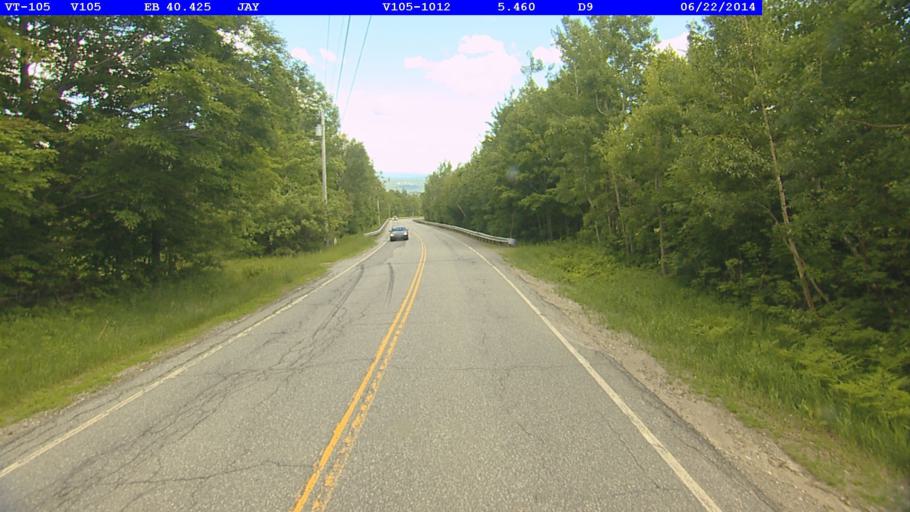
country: CA
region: Quebec
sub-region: Monteregie
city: Sutton
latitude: 44.9774
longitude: -72.4767
